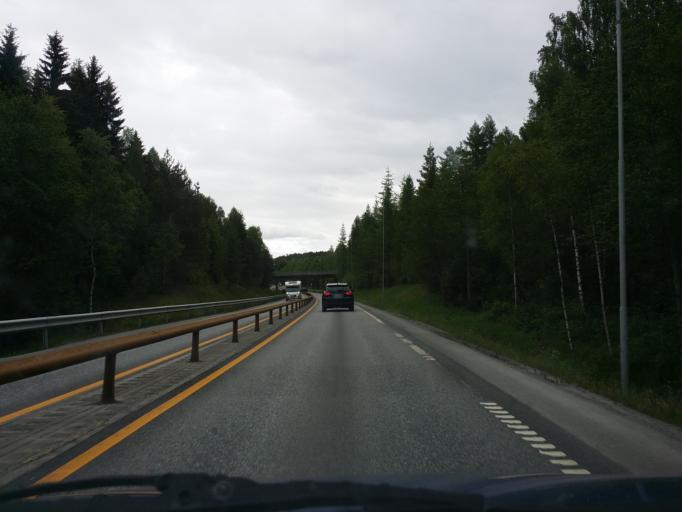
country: NO
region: Hedmark
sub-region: Ringsaker
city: Moelv
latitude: 60.9091
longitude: 10.7313
